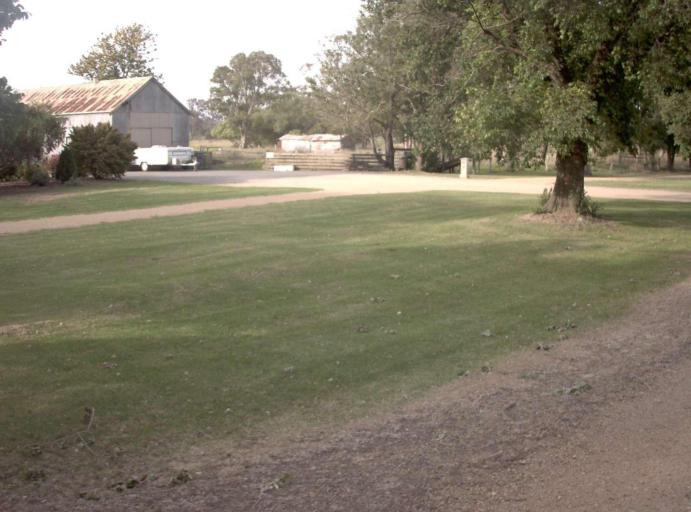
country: AU
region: Victoria
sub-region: Wellington
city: Heyfield
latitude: -37.9667
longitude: 146.9611
